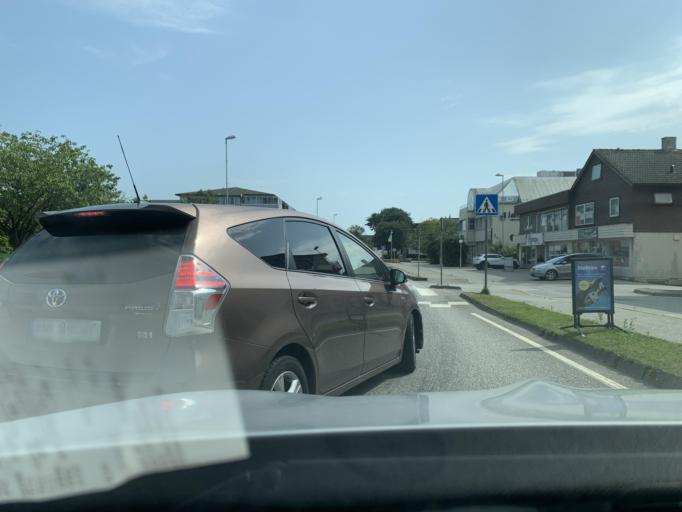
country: NO
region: Rogaland
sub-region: Klepp
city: Kleppe
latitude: 58.7743
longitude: 5.6291
